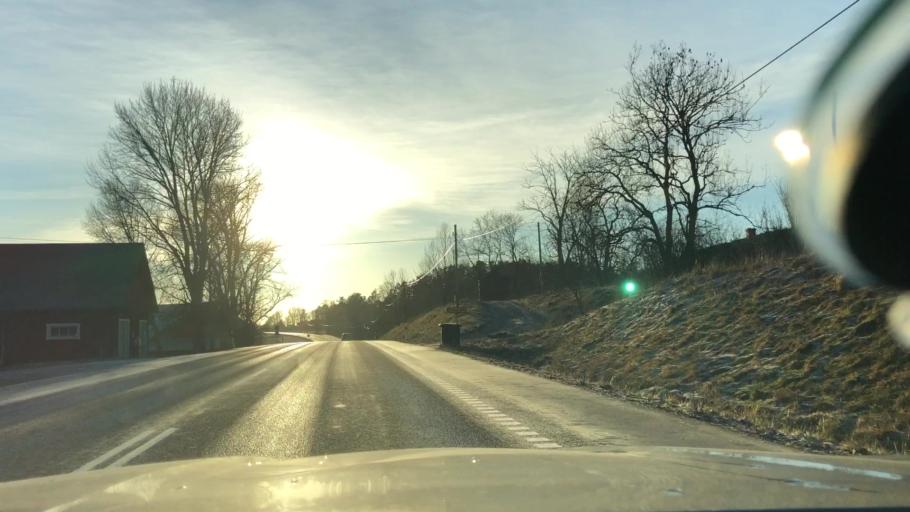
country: SE
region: Soedermanland
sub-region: Trosa Kommun
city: Vagnharad
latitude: 59.0357
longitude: 17.5994
